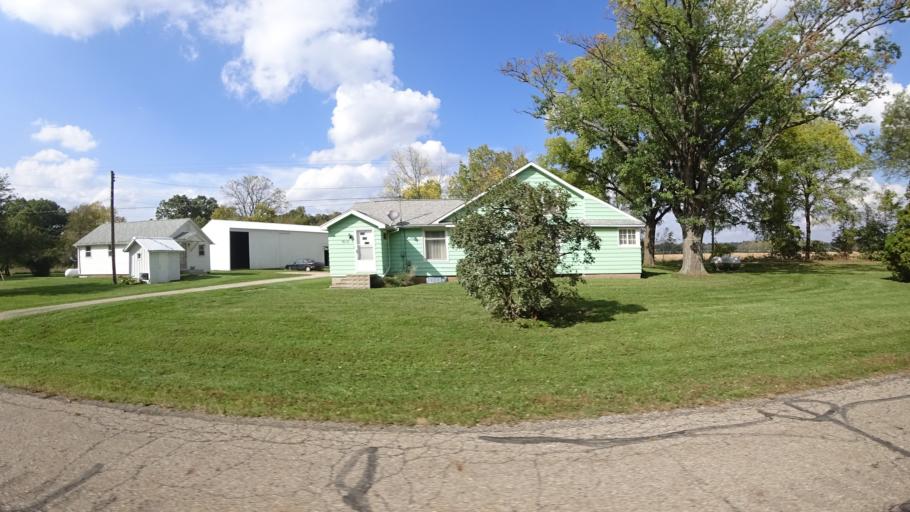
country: US
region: Michigan
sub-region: Branch County
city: Union City
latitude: 42.0869
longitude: -85.1175
